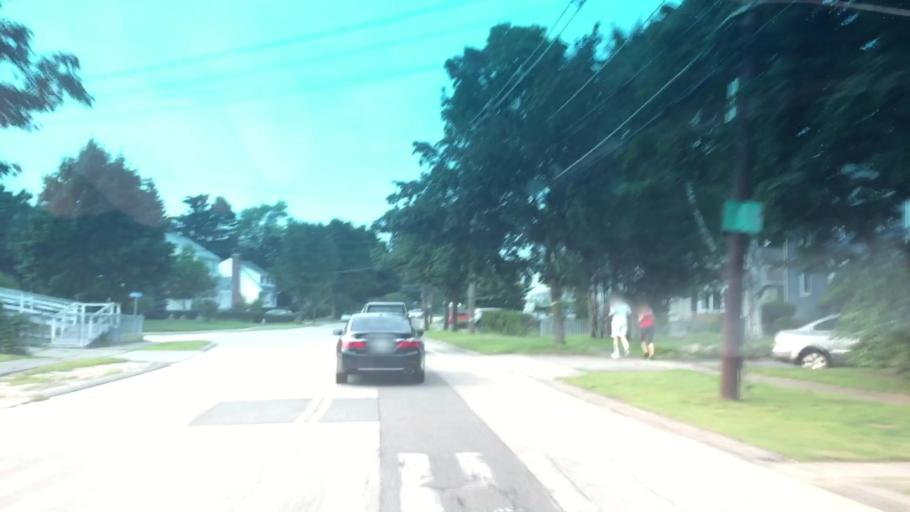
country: US
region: Massachusetts
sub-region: Norfolk County
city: Norwood
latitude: 42.1803
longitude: -71.1974
